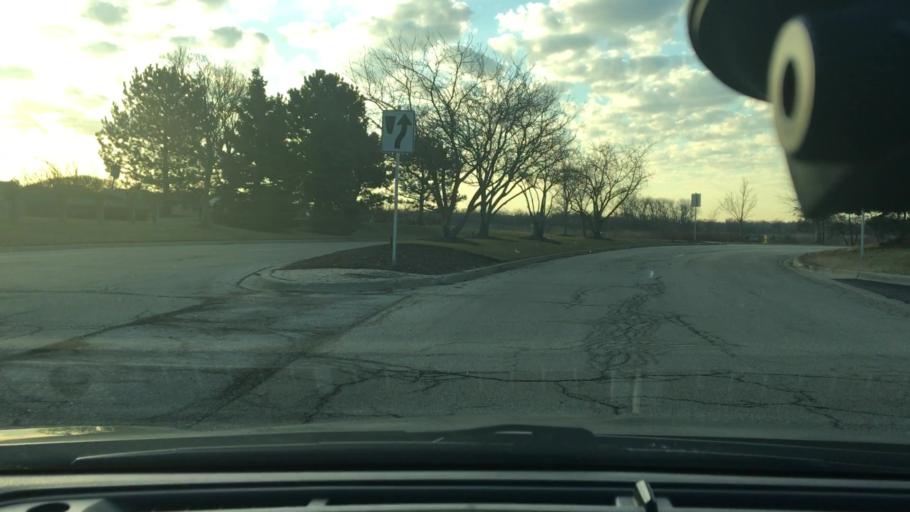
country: US
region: Illinois
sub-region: Cook County
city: Northbrook
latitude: 42.1040
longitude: -87.8107
